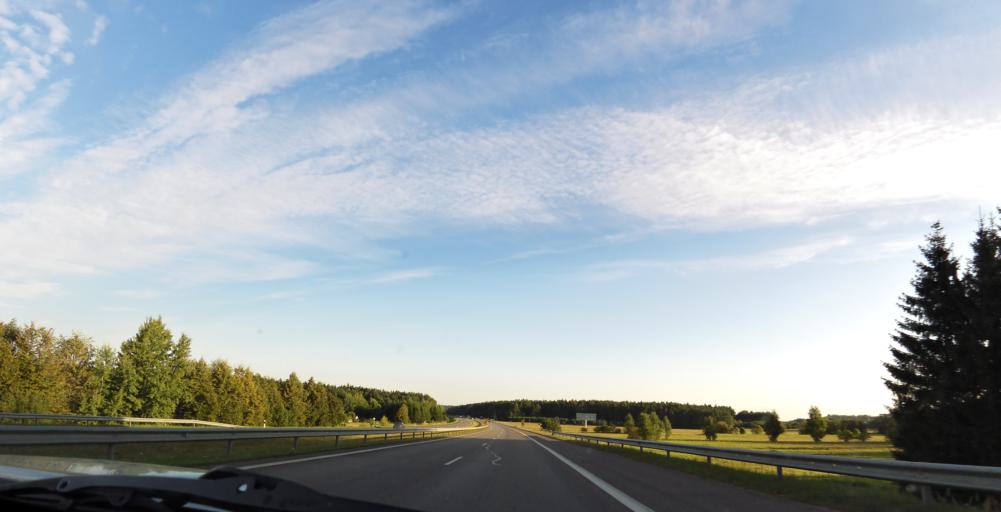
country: LT
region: Vilnius County
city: Ukmerge
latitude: 55.2365
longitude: 24.8211
